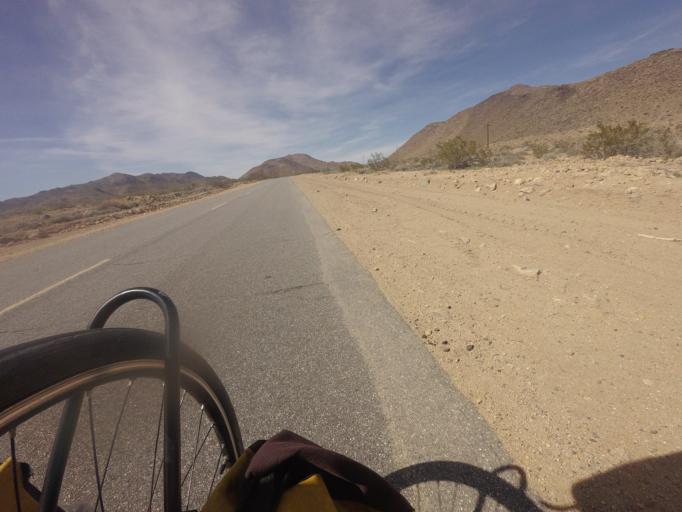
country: US
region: California
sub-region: San Bernardino County
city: Searles Valley
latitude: 35.5754
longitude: -117.4518
